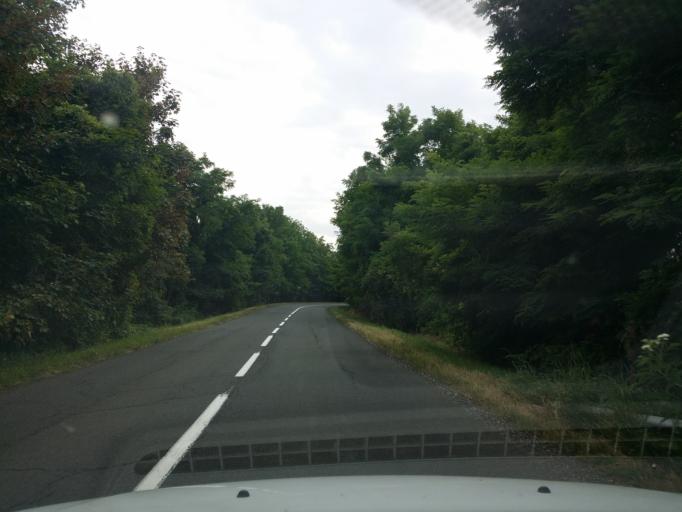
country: HU
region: Nograd
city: Bercel
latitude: 47.9308
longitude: 19.3641
